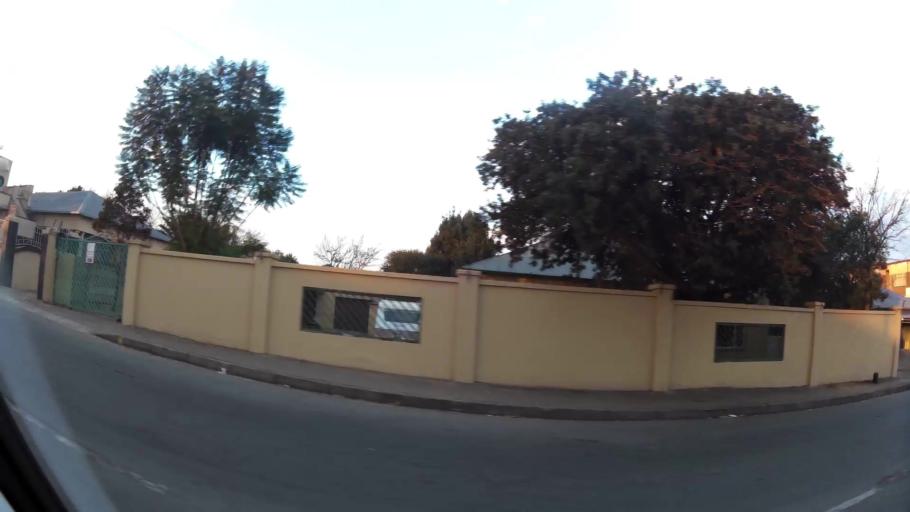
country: ZA
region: Gauteng
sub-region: Ekurhuleni Metropolitan Municipality
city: Germiston
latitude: -26.1847
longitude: 28.1701
